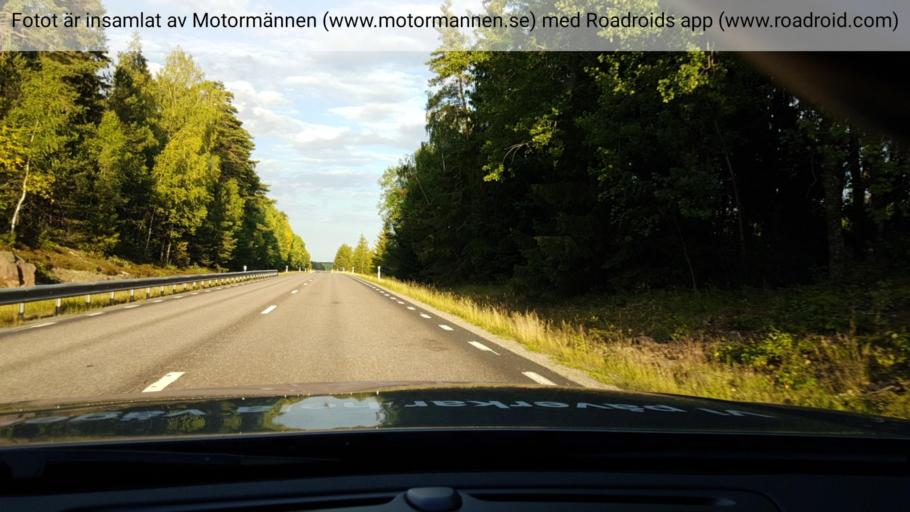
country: SE
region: Uppsala
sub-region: Enkopings Kommun
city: Orsundsbro
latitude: 59.8674
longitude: 17.3264
